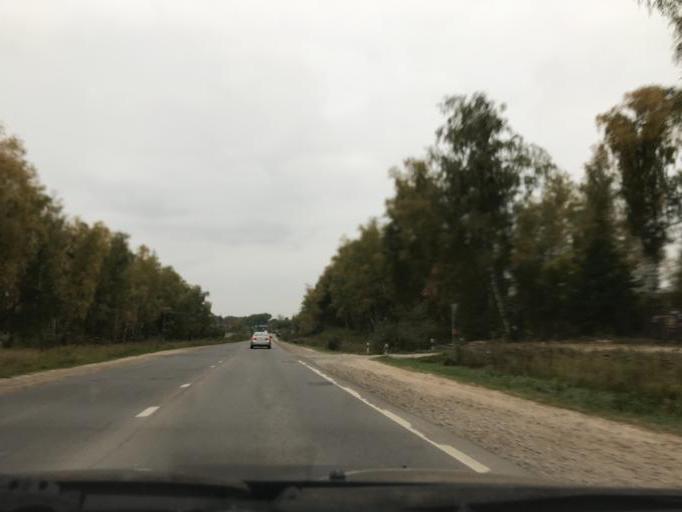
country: RU
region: Kaluga
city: Kaluga
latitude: 54.6089
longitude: 36.2712
